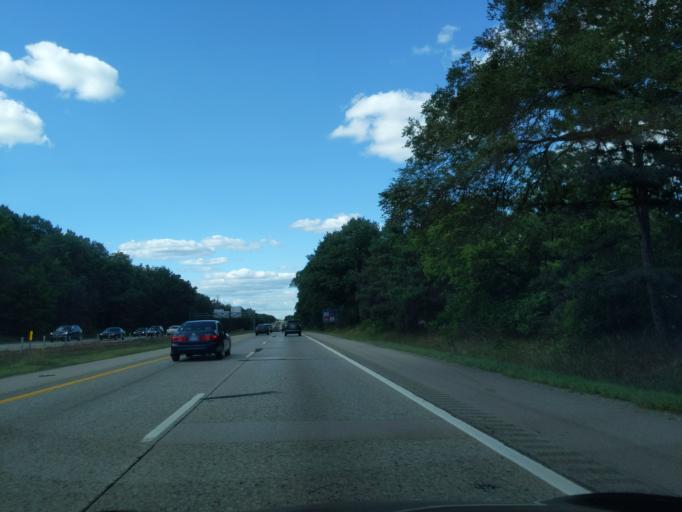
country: US
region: Michigan
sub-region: Muskegon County
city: Muskegon Heights
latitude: 43.1820
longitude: -86.2049
